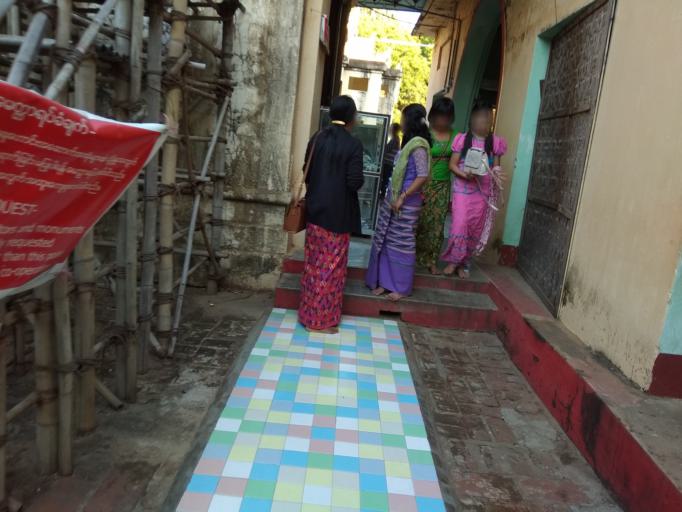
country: MM
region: Magway
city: Chauk
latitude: 21.1571
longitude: 94.8613
